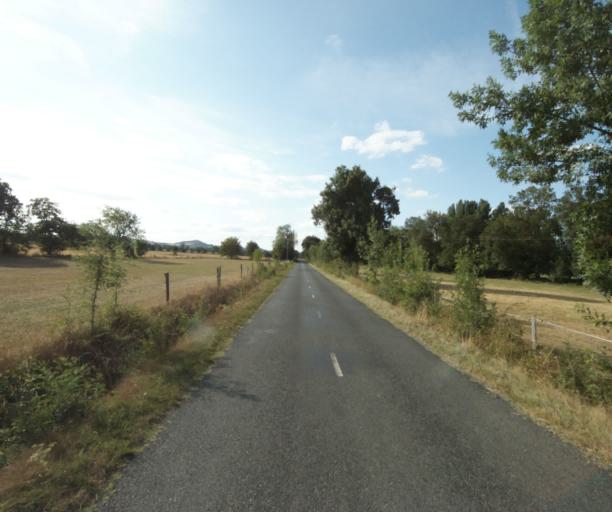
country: FR
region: Midi-Pyrenees
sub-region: Departement de la Haute-Garonne
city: Revel
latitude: 43.4852
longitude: 1.9852
